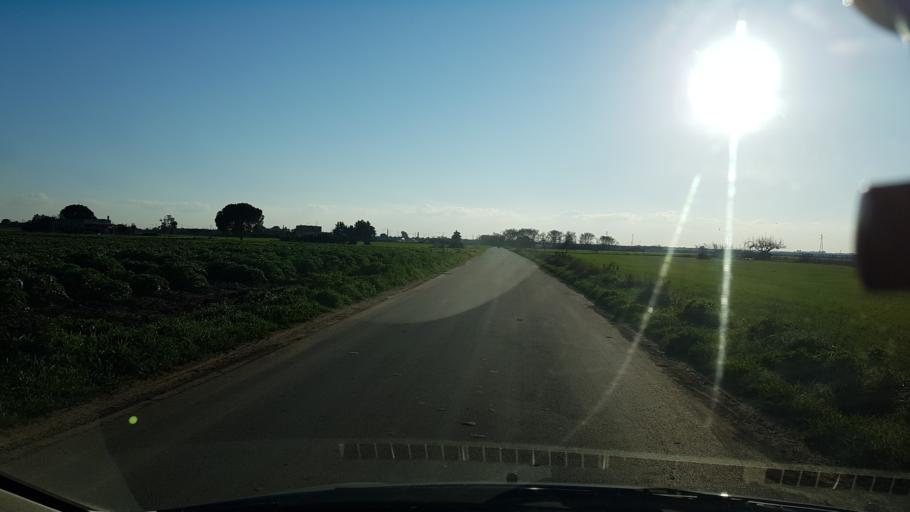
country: IT
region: Apulia
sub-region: Provincia di Brindisi
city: Brindisi
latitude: 40.5878
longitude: 17.8909
